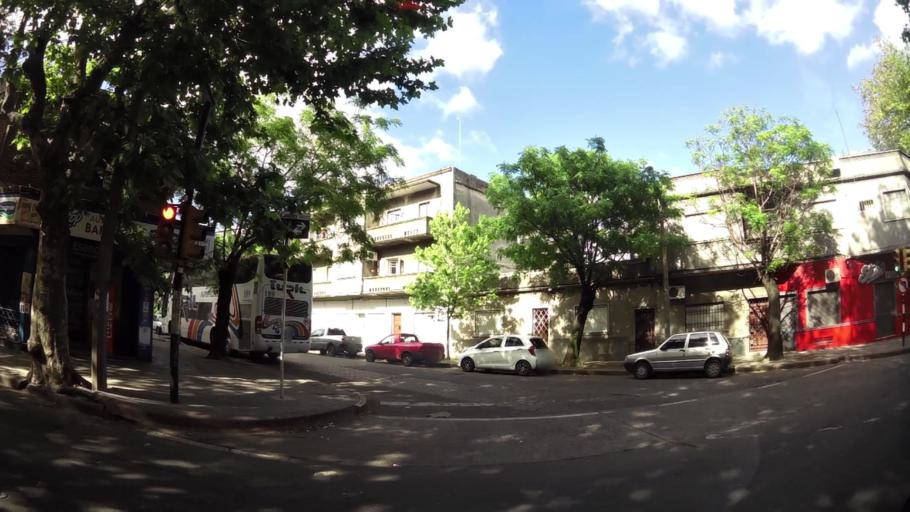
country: UY
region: Montevideo
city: Montevideo
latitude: -34.8784
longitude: -56.1748
